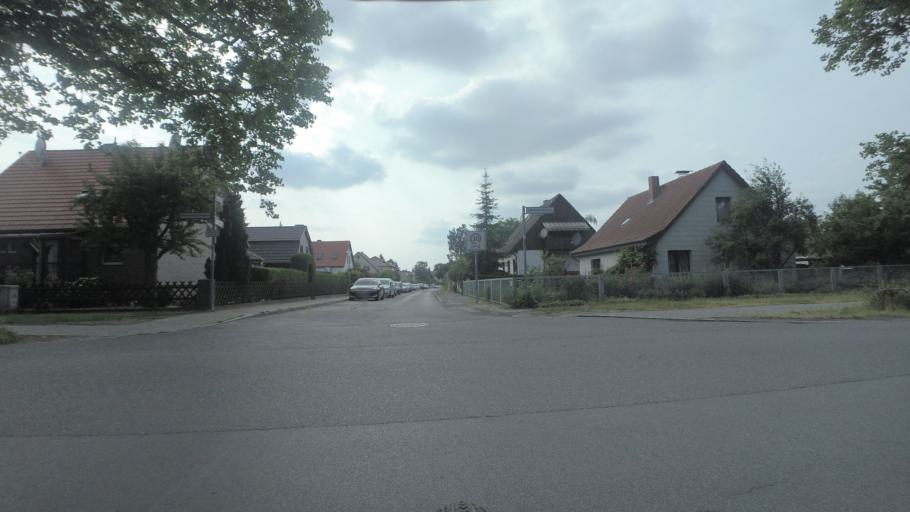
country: DE
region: Berlin
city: Rudow
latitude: 52.4050
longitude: 13.4909
